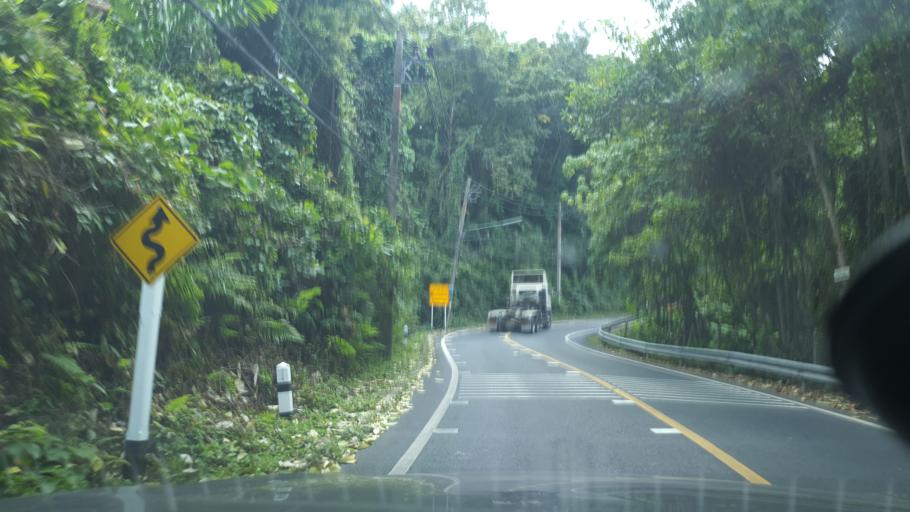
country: TH
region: Phuket
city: Thalang
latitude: 8.0408
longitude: 98.2762
